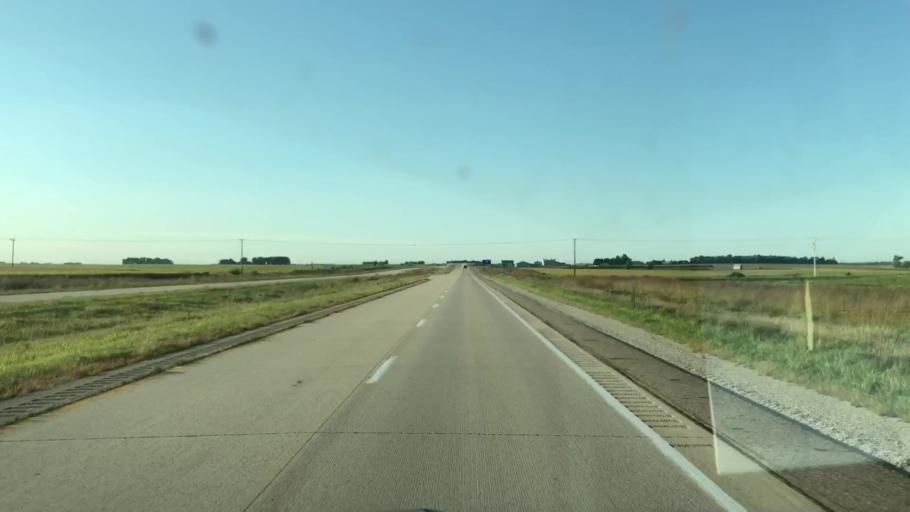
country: US
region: Iowa
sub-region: Osceola County
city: Sibley
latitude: 43.4492
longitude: -95.7137
